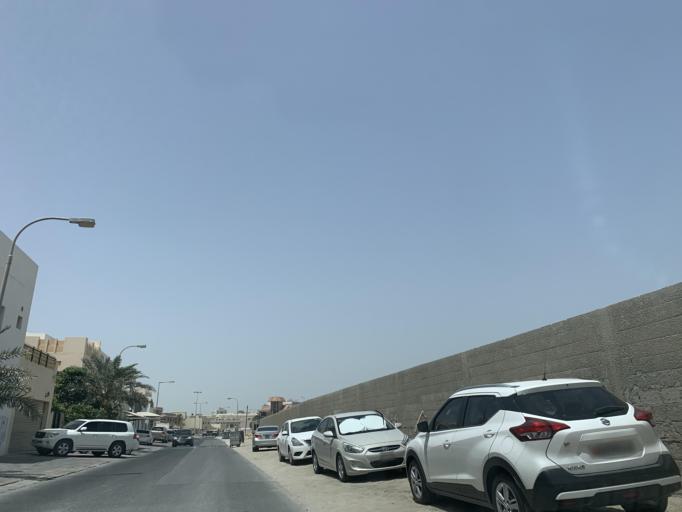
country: BH
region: Northern
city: Madinat `Isa
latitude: 26.1570
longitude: 50.5795
